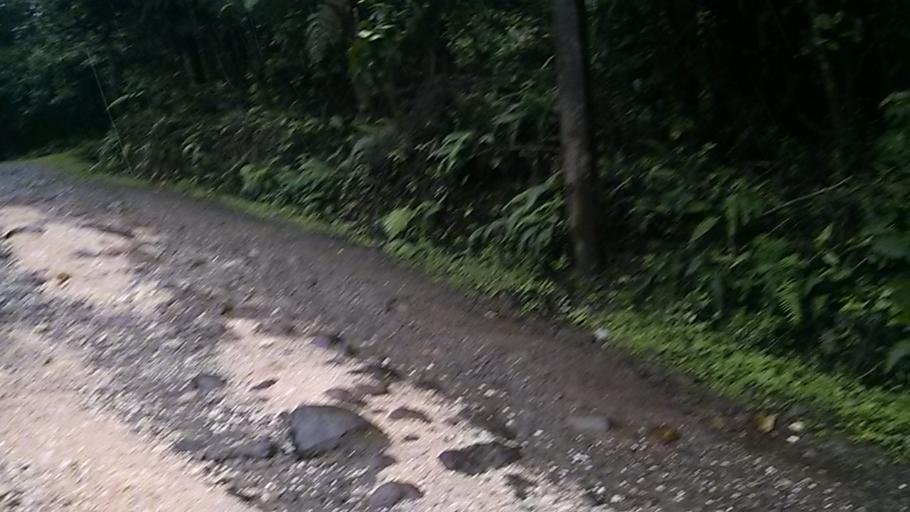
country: CR
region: San Jose
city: Ipis
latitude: 10.0268
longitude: -83.9419
